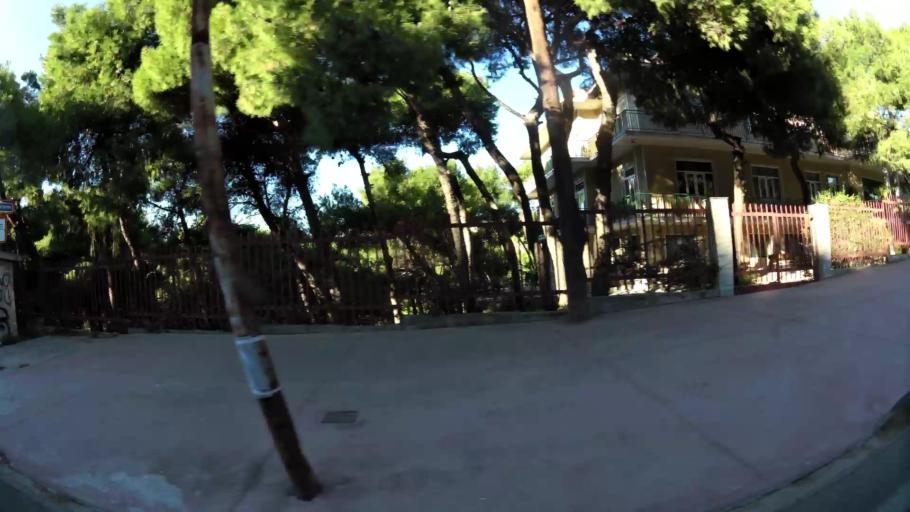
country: GR
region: Attica
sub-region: Nomarchia Athinas
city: Nea Penteli
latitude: 38.0524
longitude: 23.8502
